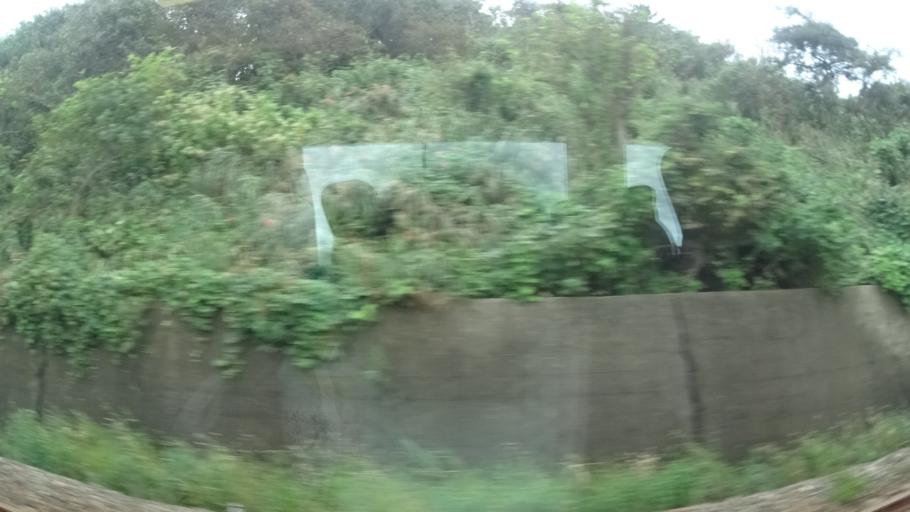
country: JP
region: Niigata
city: Murakami
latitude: 38.5264
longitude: 139.5407
